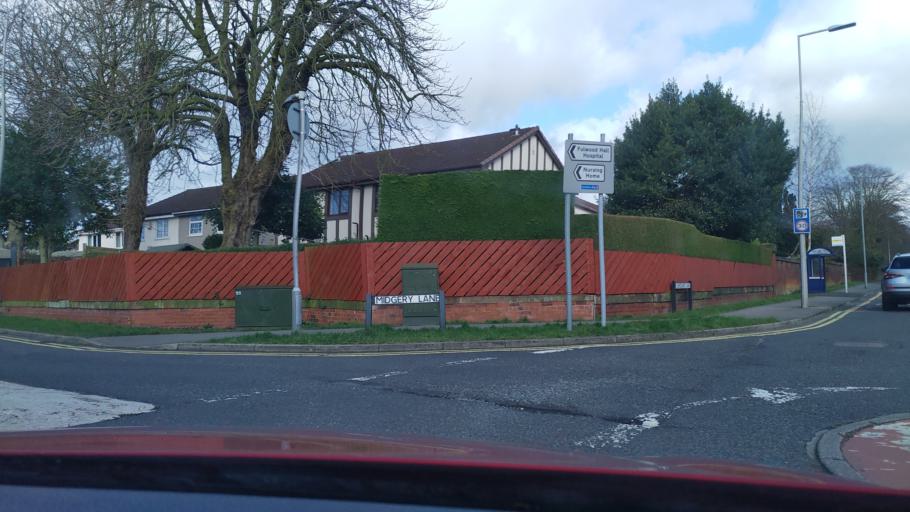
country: GB
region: England
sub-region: Lancashire
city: Goosnargh
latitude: 53.7856
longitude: -2.6825
